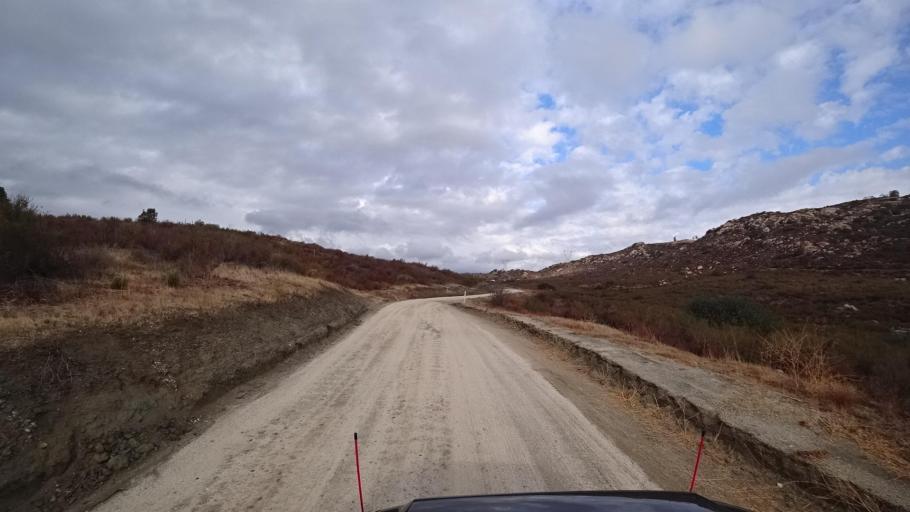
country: MX
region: Baja California
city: Tecate
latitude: 32.5912
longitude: -116.6261
